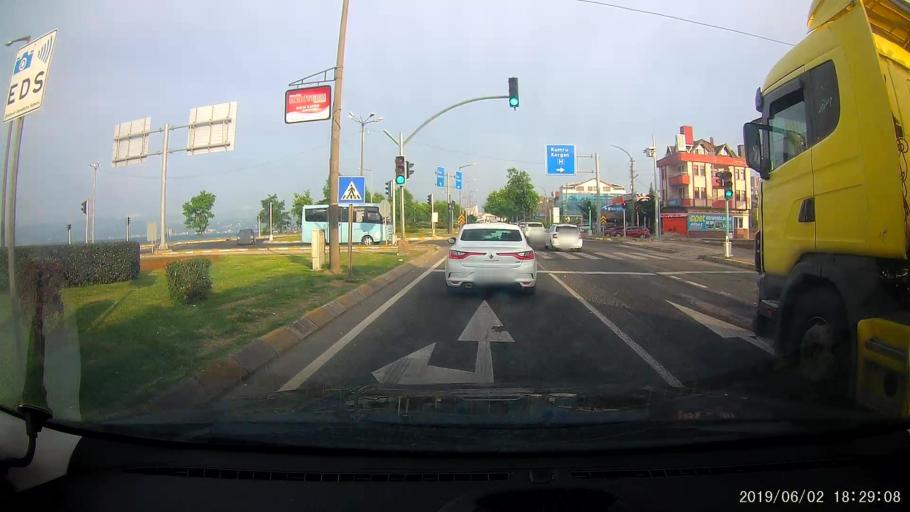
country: TR
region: Ordu
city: Fatsa
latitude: 41.0399
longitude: 37.4892
